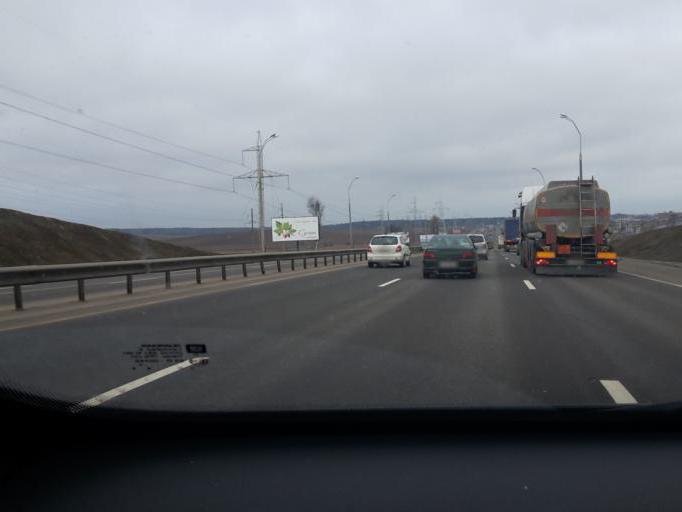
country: BY
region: Minsk
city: Novoye Medvezhino
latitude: 53.8856
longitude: 27.4154
